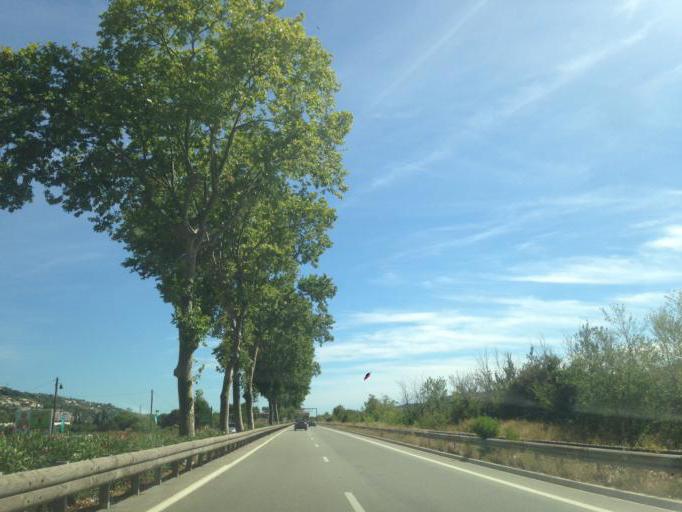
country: FR
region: Provence-Alpes-Cote d'Azur
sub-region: Departement des Alpes-Maritimes
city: Gattieres
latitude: 43.7339
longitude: 7.1845
